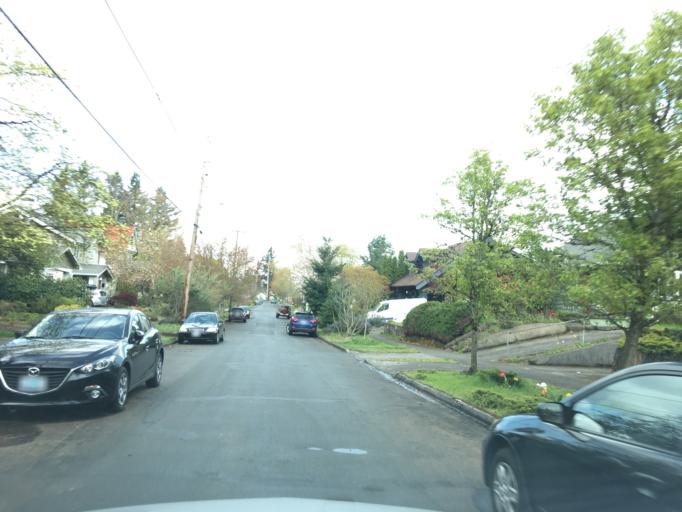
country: US
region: Oregon
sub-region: Multnomah County
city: Lents
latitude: 45.5457
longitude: -122.5994
